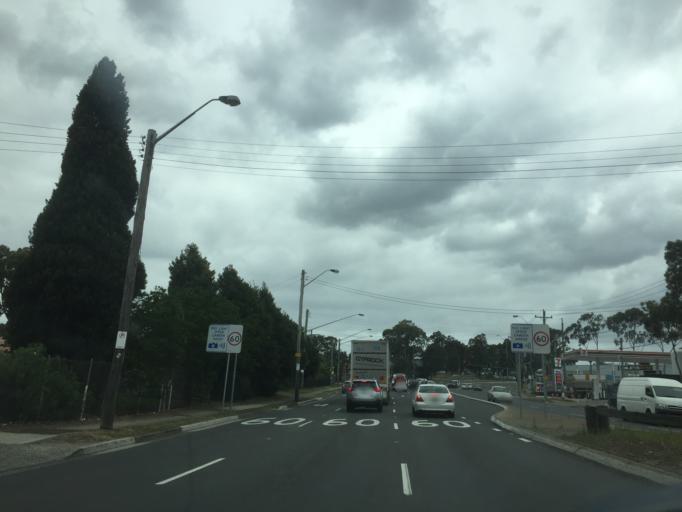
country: AU
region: New South Wales
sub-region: Blacktown
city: Blacktown
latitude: -33.7693
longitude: 150.9418
